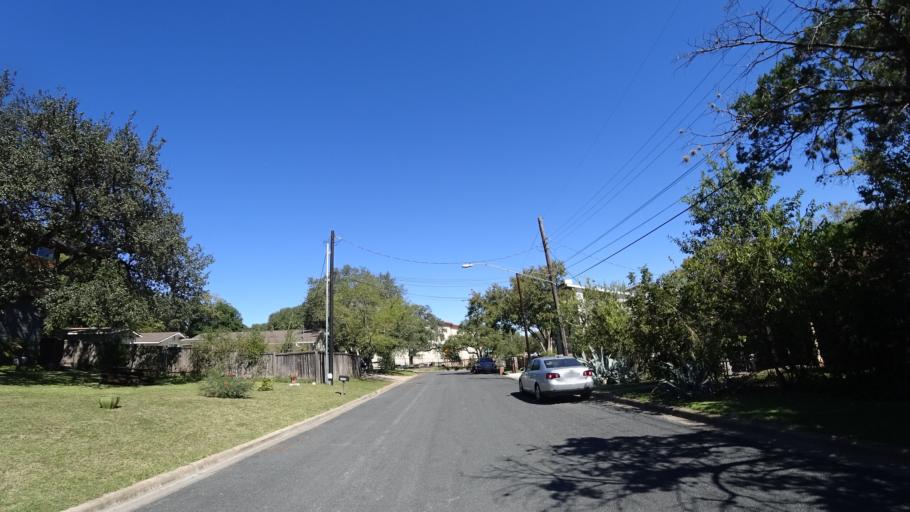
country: US
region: Texas
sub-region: Travis County
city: Austin
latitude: 30.2394
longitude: -97.7624
